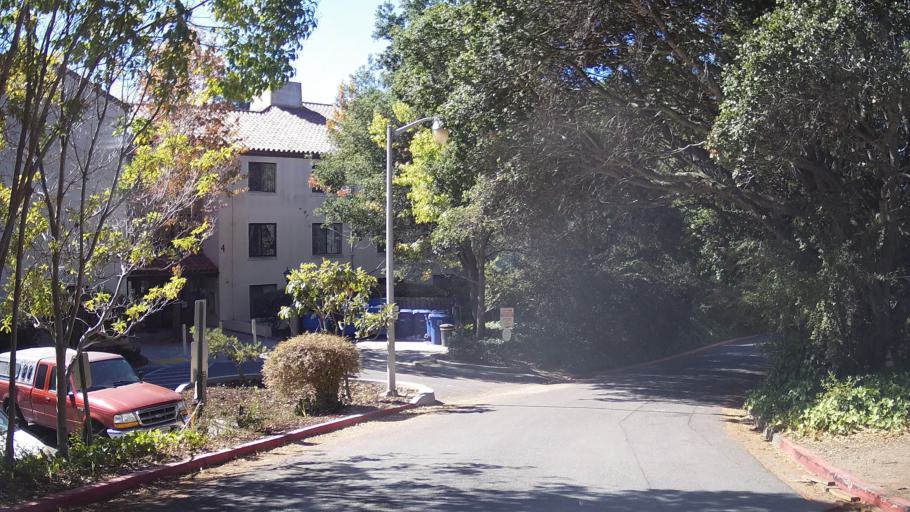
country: US
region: California
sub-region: Alameda County
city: Berkeley
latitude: 37.8638
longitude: -122.2468
